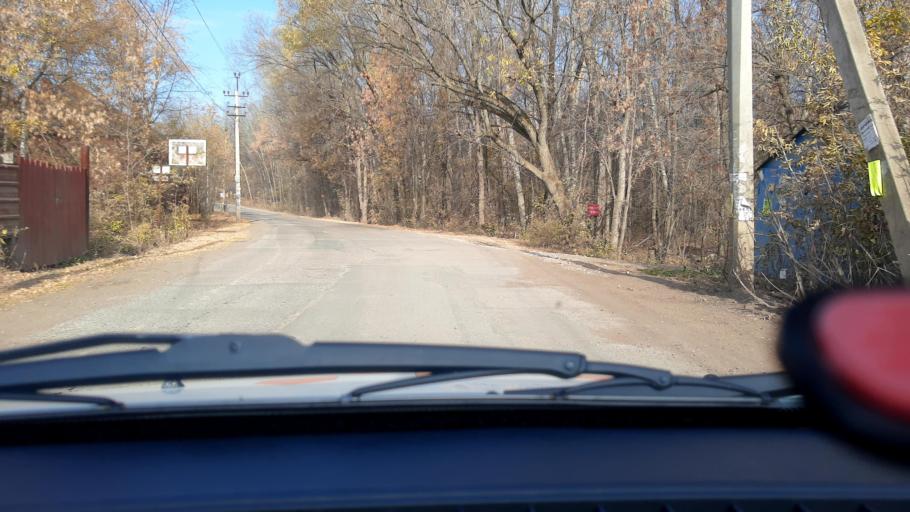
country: RU
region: Bashkortostan
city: Ufa
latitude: 54.6966
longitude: 55.9024
